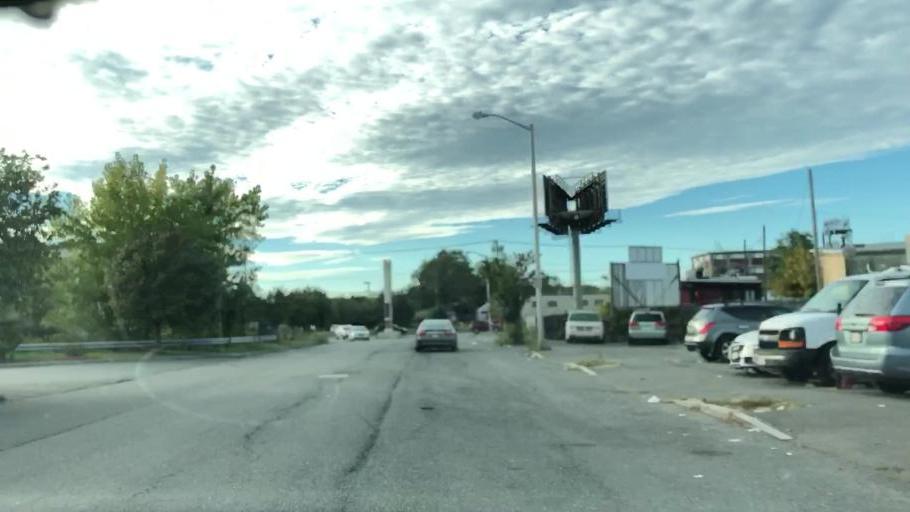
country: US
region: Massachusetts
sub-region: Suffolk County
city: Revere
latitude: 42.4014
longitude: -71.0036
